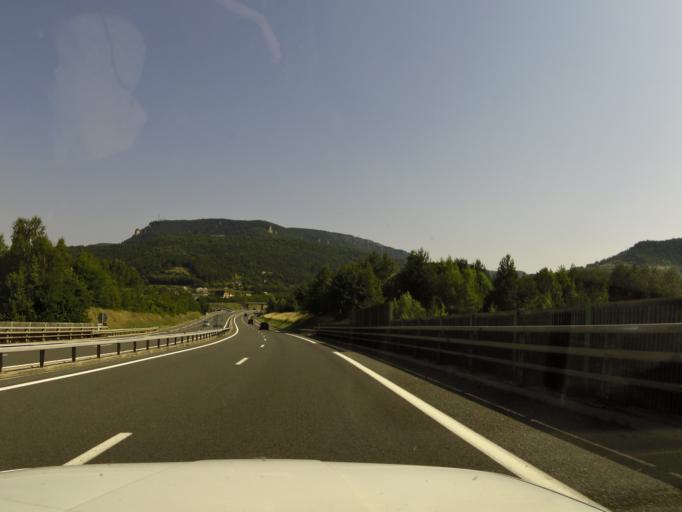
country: FR
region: Languedoc-Roussillon
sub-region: Departement de la Lozere
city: La Canourgue
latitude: 44.4417
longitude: 3.1937
